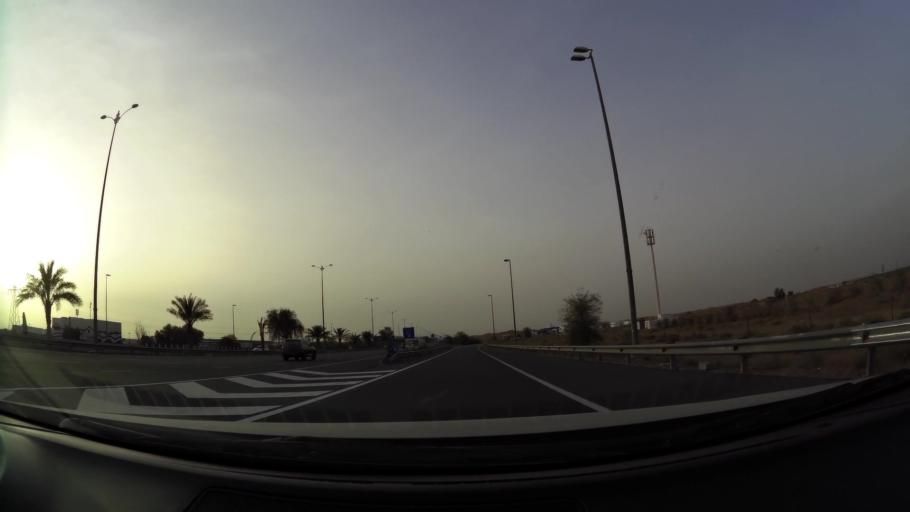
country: OM
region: Al Buraimi
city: Al Buraymi
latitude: 24.3974
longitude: 55.7968
